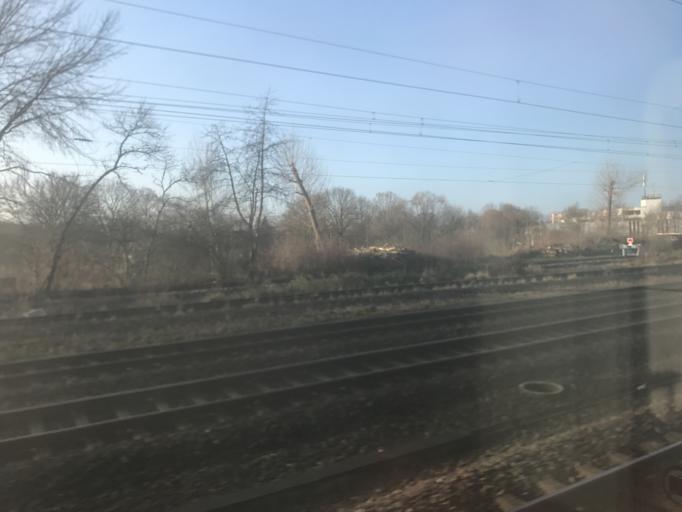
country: DE
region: North Rhine-Westphalia
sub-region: Regierungsbezirk Dusseldorf
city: Erkrath
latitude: 51.1926
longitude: 6.8458
